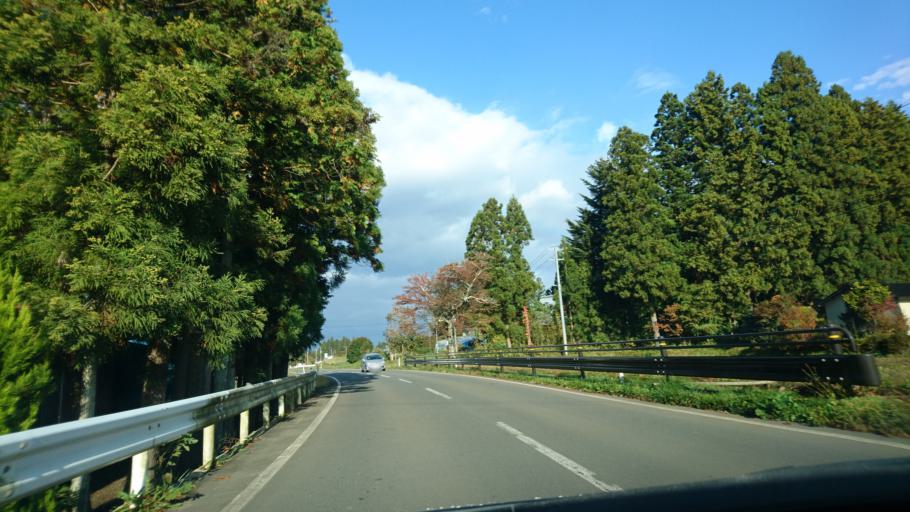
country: JP
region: Iwate
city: Mizusawa
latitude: 39.0484
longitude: 141.0503
